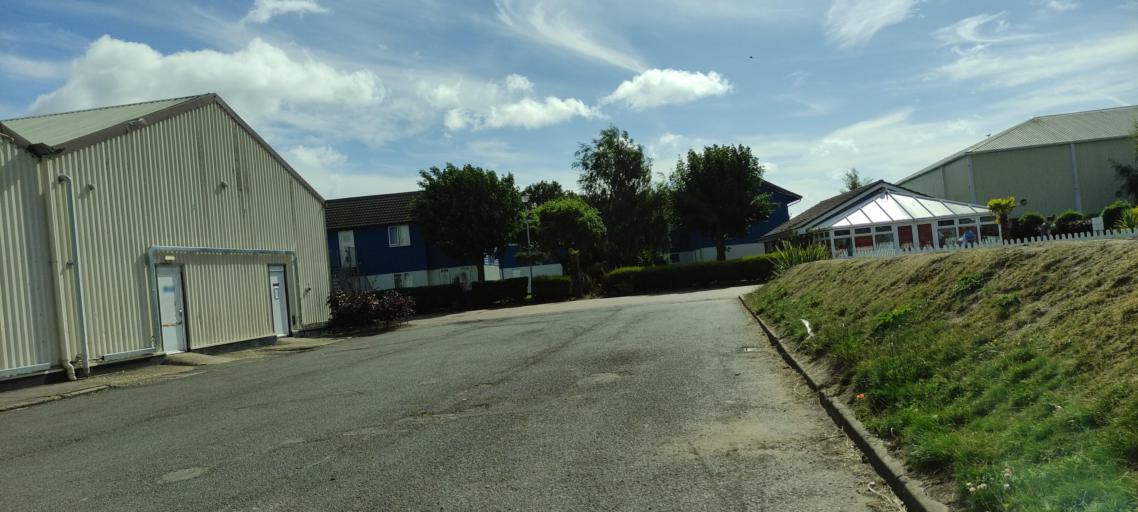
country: GB
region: England
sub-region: Lincolnshire
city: Ingoldmells
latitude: 53.1832
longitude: 0.3505
